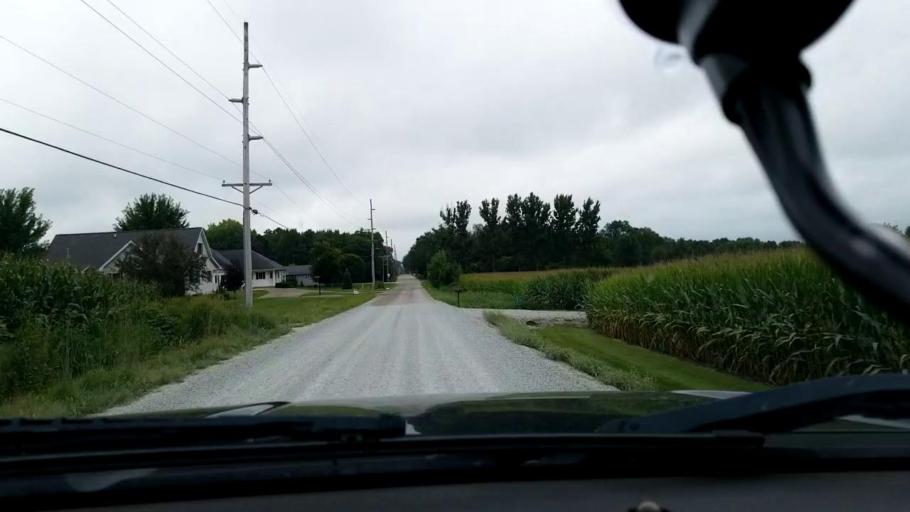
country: US
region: Iowa
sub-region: Buchanan County
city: Independence
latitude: 42.4854
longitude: -91.8846
